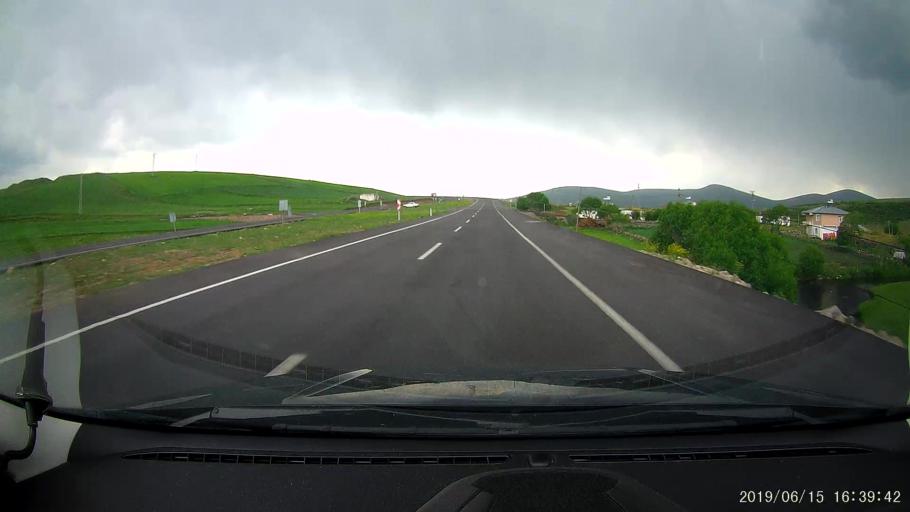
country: TR
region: Ardahan
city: Haskoy
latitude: 40.9800
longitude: 42.8954
